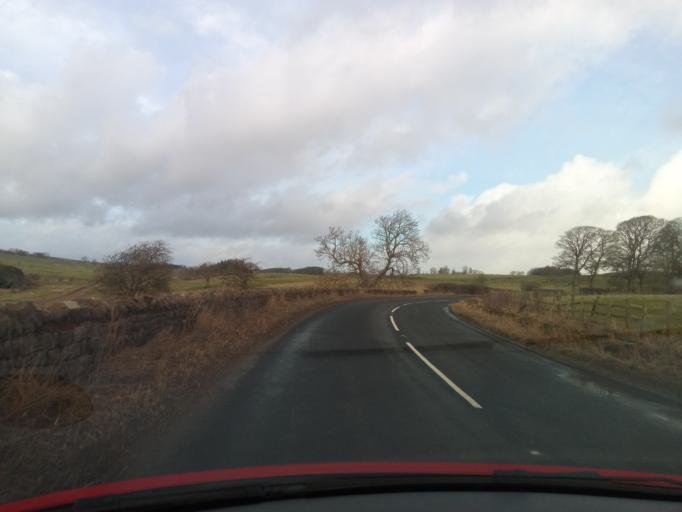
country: GB
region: England
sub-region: Northumberland
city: Rothley
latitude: 55.1038
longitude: -2.0186
